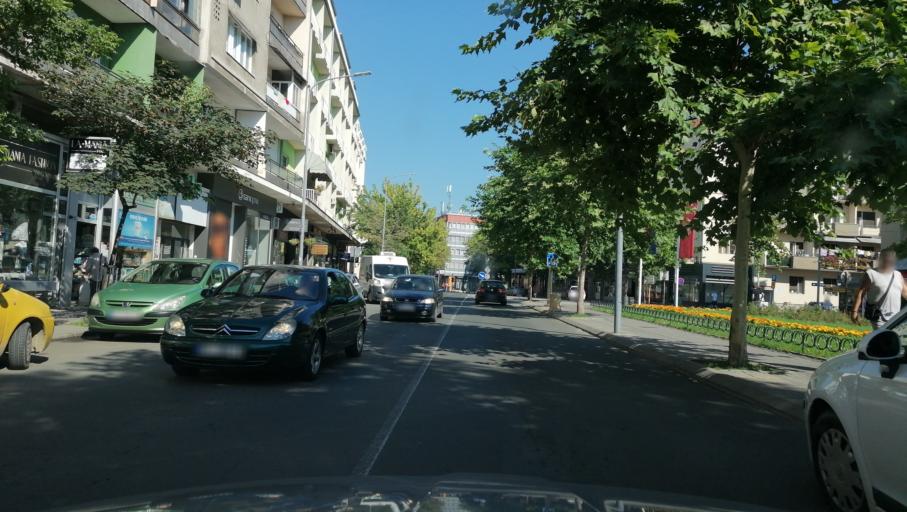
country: RS
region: Central Serbia
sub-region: Rasinski Okrug
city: Krusevac
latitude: 43.5794
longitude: 21.3310
